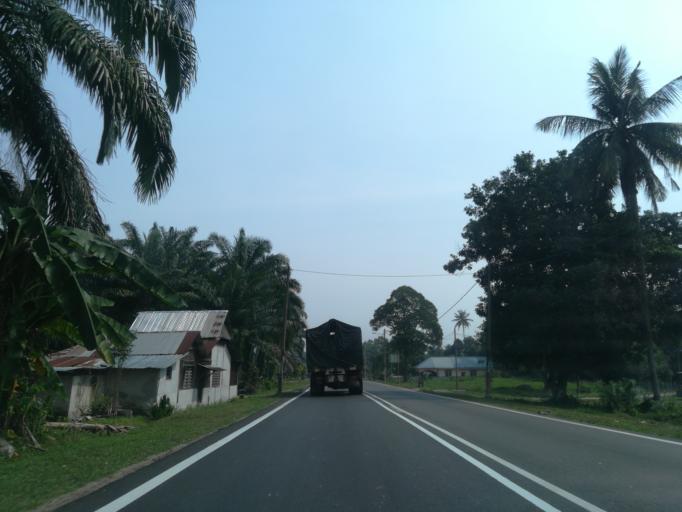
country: MY
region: Penang
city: Tasek Glugor
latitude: 5.4601
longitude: 100.5470
